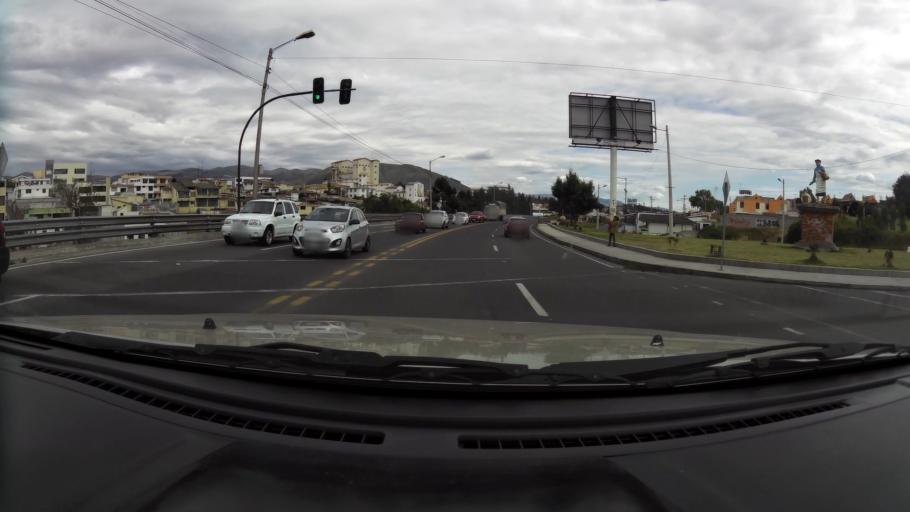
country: EC
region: Cotopaxi
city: Latacunga
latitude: -0.9263
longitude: -78.6252
